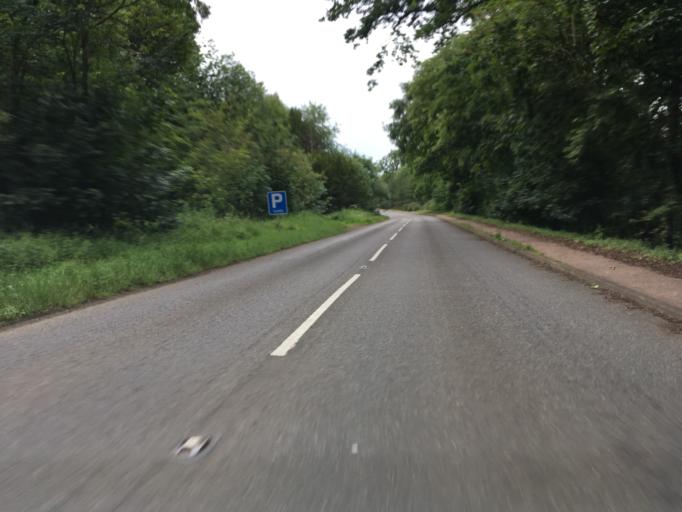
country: GB
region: England
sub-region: Central Bedfordshire
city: Aspley Guise
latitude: 51.9980
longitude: -0.6358
